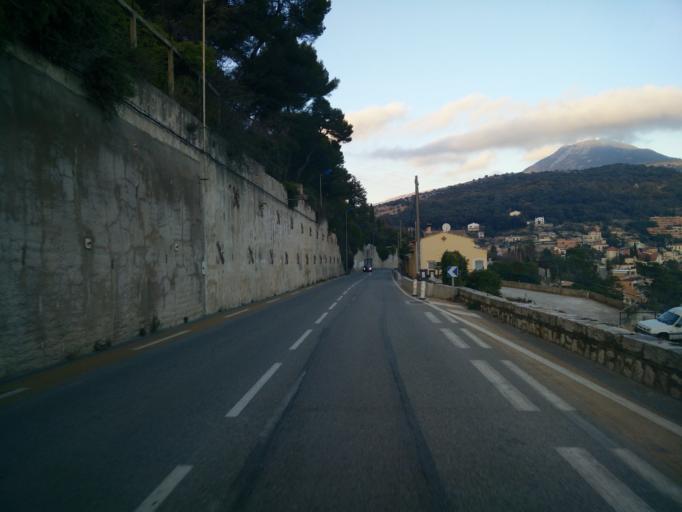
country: FR
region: Provence-Alpes-Cote d'Azur
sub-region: Departement des Alpes-Maritimes
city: La Turbie
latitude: 43.7411
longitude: 7.3907
